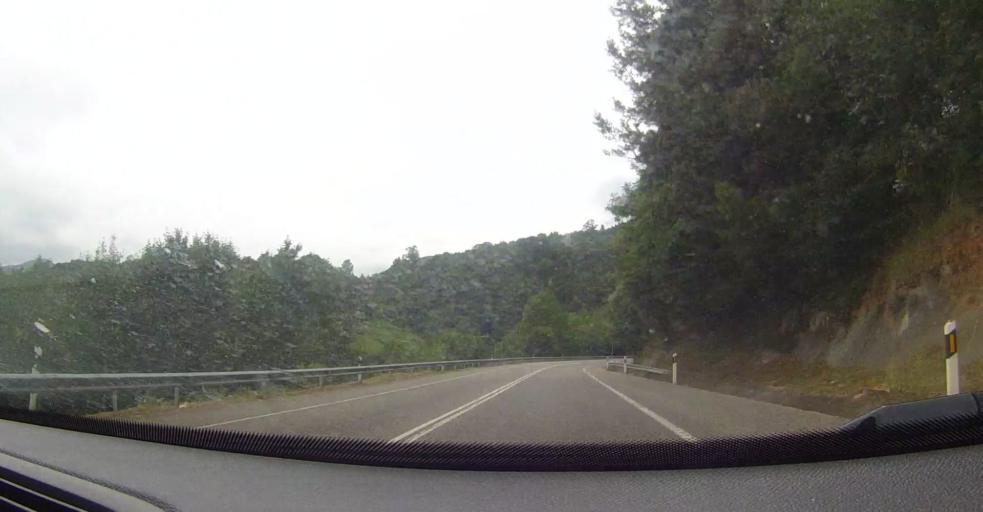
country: ES
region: Asturias
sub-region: Province of Asturias
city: Pilona
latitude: 43.3531
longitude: -5.3737
